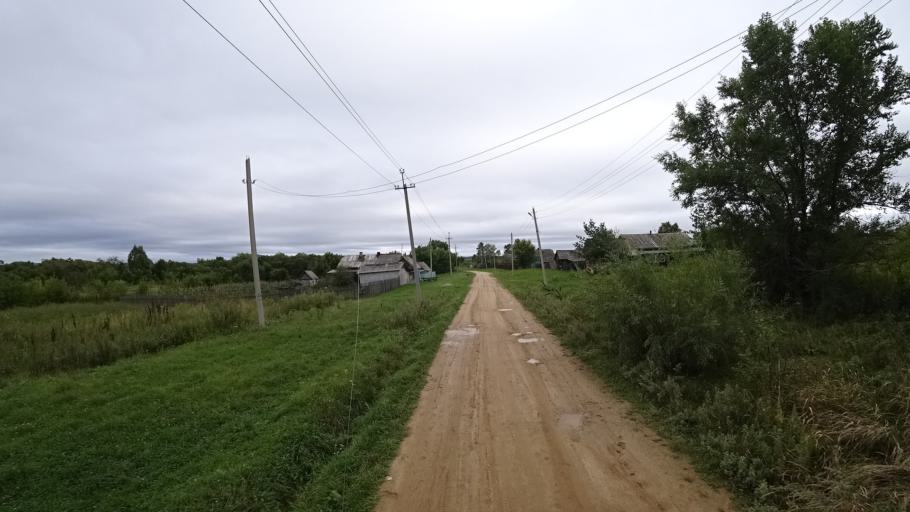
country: RU
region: Primorskiy
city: Rettikhovka
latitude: 44.1408
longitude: 132.6415
